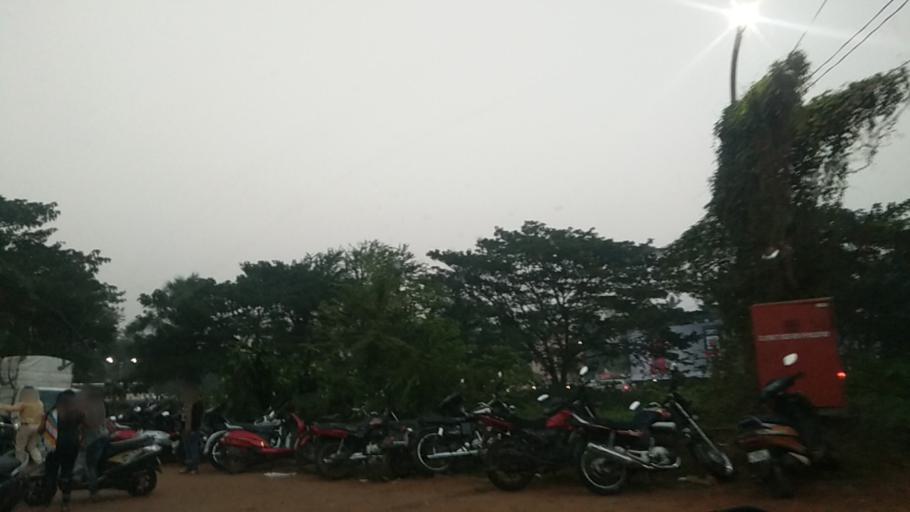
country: IN
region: Goa
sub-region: South Goa
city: Madgaon
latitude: 15.2840
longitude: 73.9560
